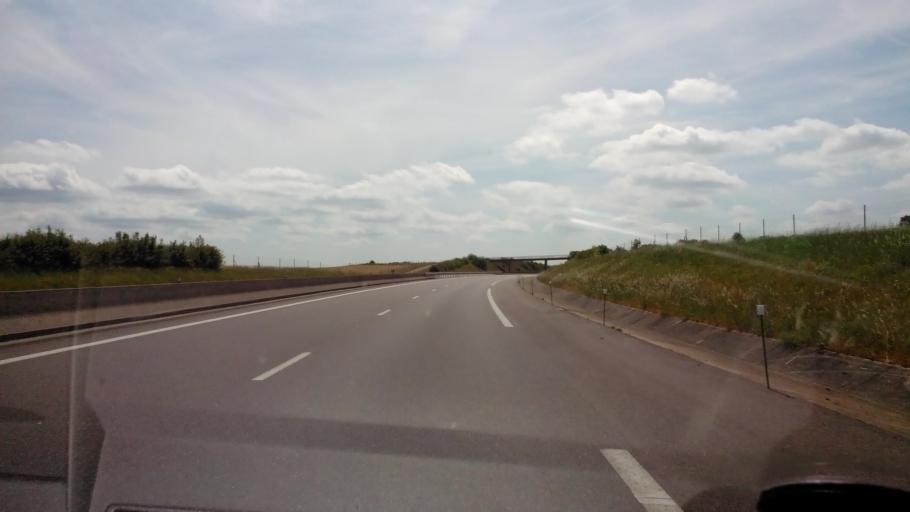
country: FR
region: Lorraine
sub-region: Departement des Vosges
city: Chatenois
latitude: 48.4048
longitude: 5.8771
